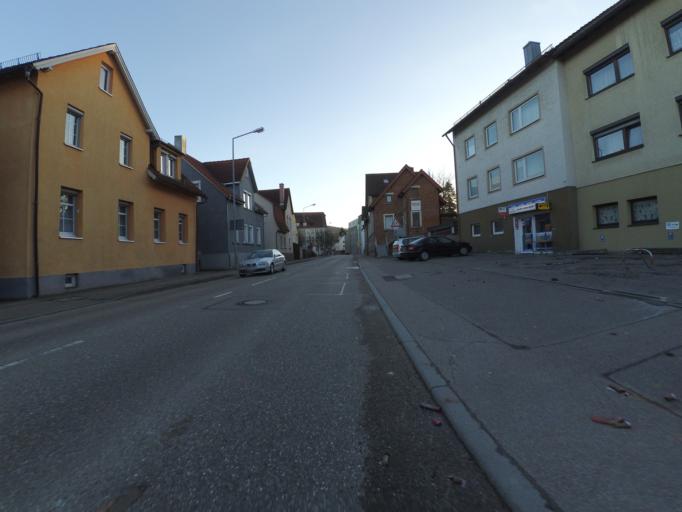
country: DE
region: Baden-Wuerttemberg
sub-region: Regierungsbezirk Stuttgart
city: Aalen
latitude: 48.8403
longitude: 10.0889
